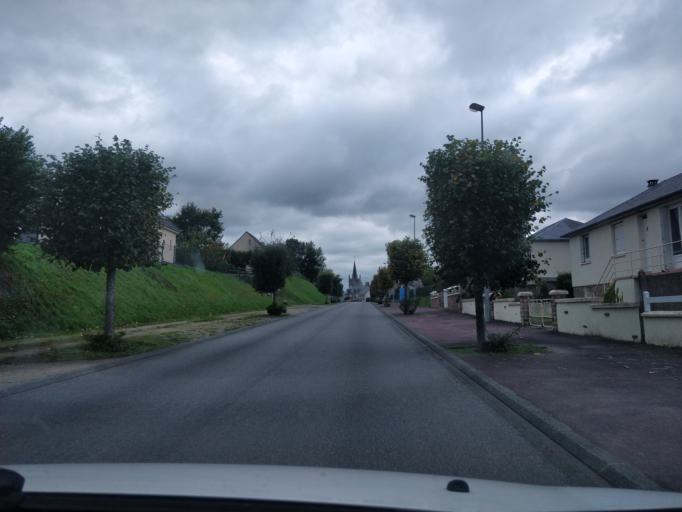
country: FR
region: Lower Normandy
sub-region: Departement de la Manche
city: Villedieu-les-Poeles
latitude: 48.8349
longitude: -1.1863
